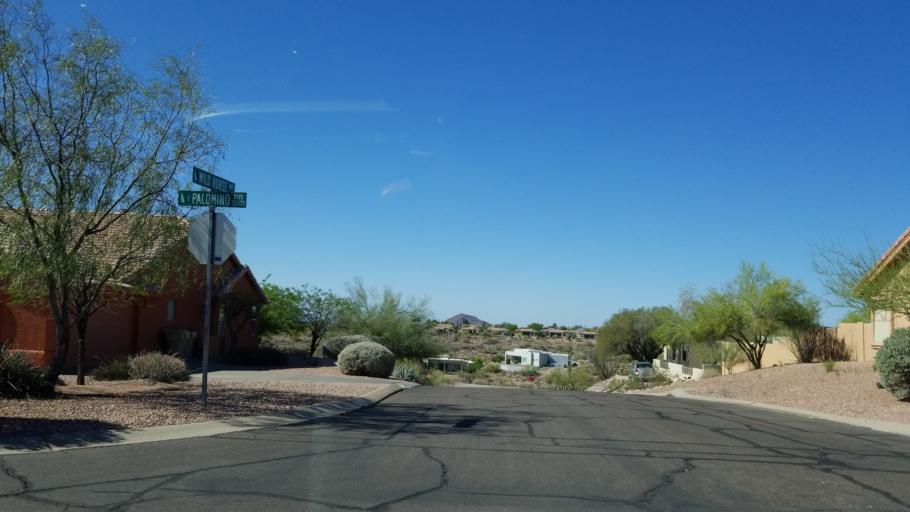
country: US
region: Arizona
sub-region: Maricopa County
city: Fountain Hills
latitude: 33.5916
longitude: -111.7492
